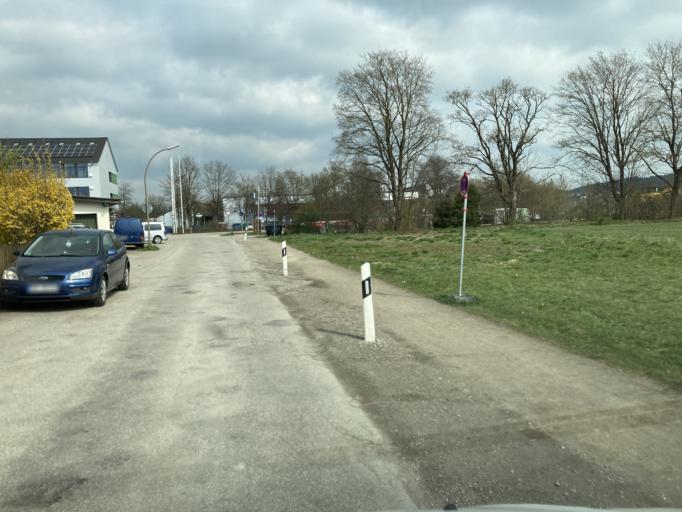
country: DE
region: Bavaria
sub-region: Upper Bavaria
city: Grafing bei Munchen
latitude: 48.0490
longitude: 11.9731
